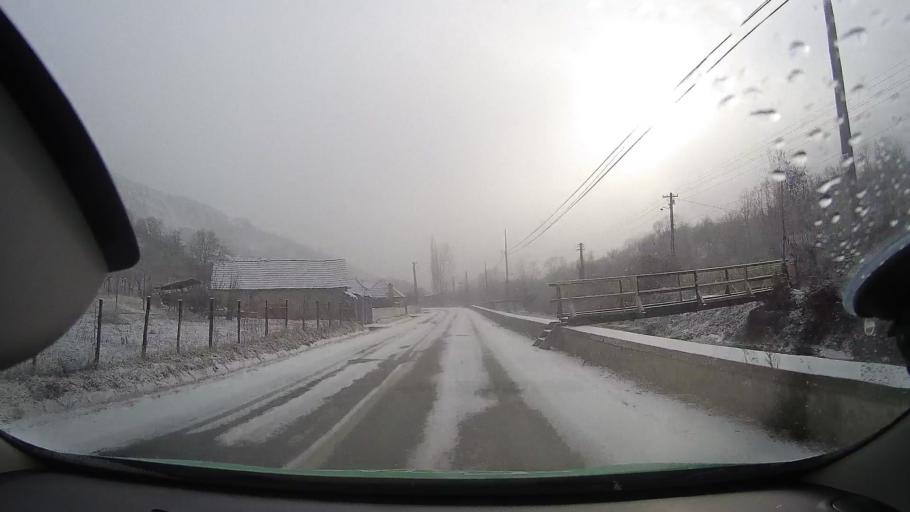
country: RO
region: Alba
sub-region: Comuna Livezile
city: Livezile
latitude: 46.3629
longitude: 23.6090
